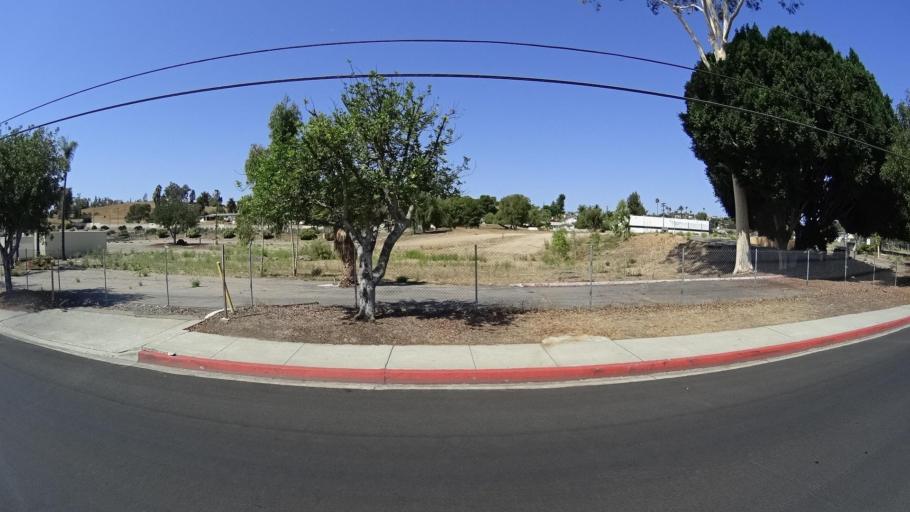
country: US
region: California
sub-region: San Diego County
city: Granite Hills
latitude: 32.8109
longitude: -116.9196
